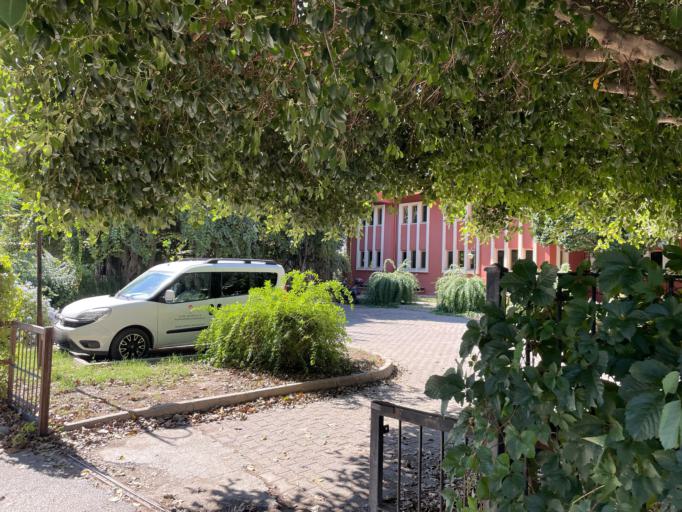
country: TR
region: Antalya
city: Kemer
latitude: 36.5966
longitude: 30.5660
